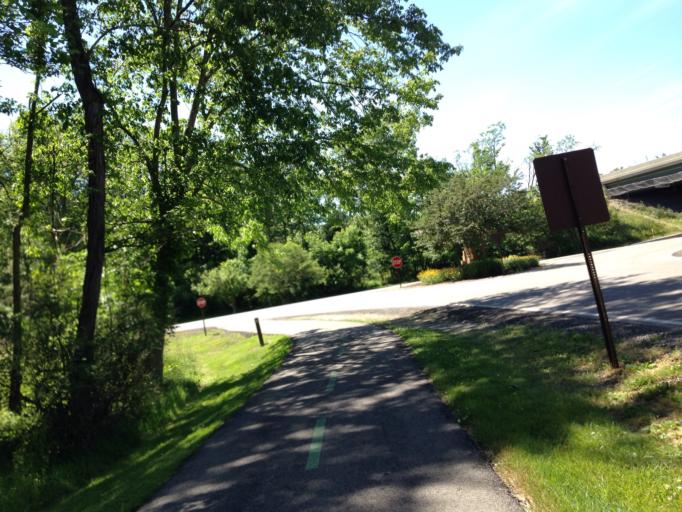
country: US
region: Ohio
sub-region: Cuyahoga County
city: Strongsville
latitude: 41.3418
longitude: -81.8354
